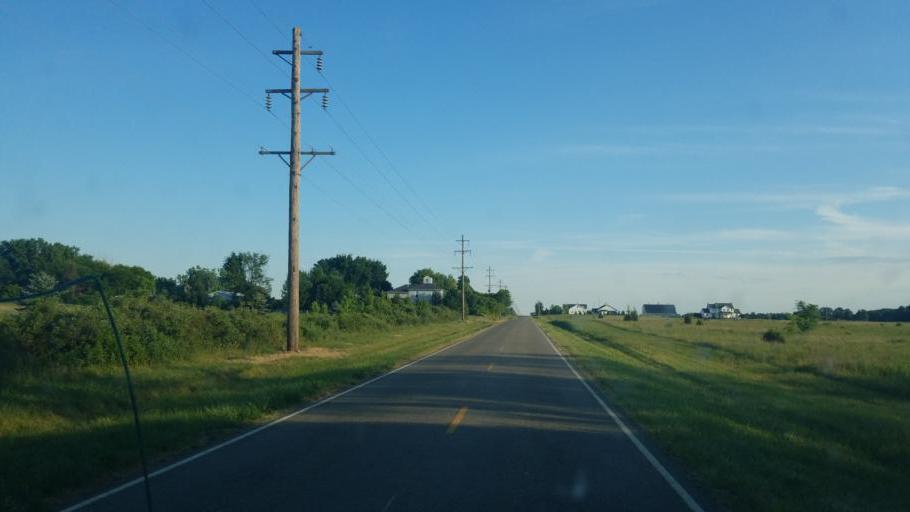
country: US
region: Ohio
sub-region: Defiance County
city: Hicksville
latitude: 41.3719
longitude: -84.7671
